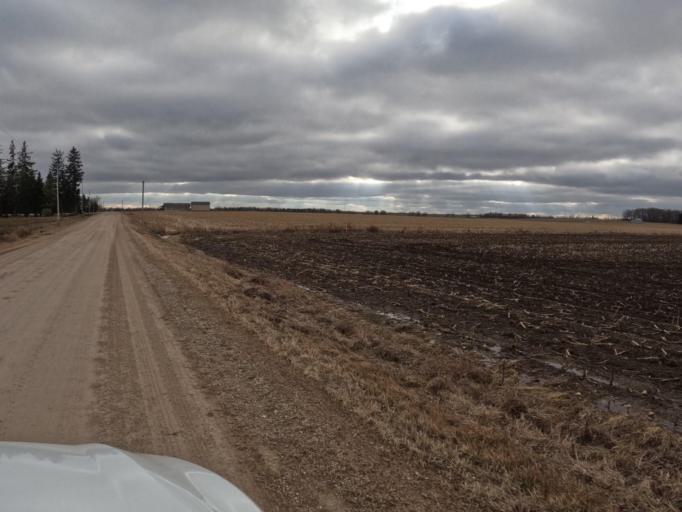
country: CA
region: Ontario
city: Shelburne
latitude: 43.8662
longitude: -80.4010
